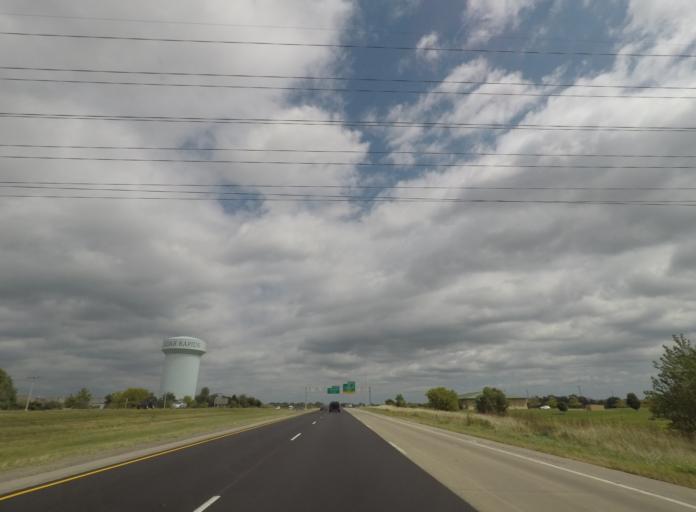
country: US
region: Iowa
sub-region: Linn County
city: Cedar Rapids
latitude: 41.9268
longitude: -91.6471
